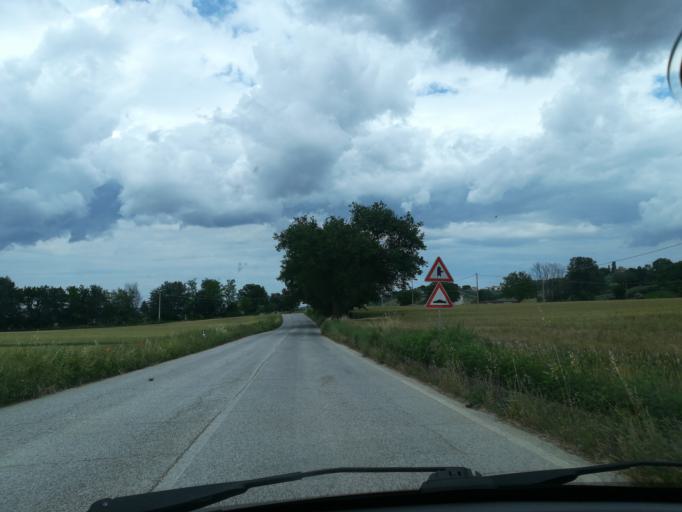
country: IT
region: The Marches
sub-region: Provincia di Macerata
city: Zona Industriale
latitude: 43.2421
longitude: 13.4765
